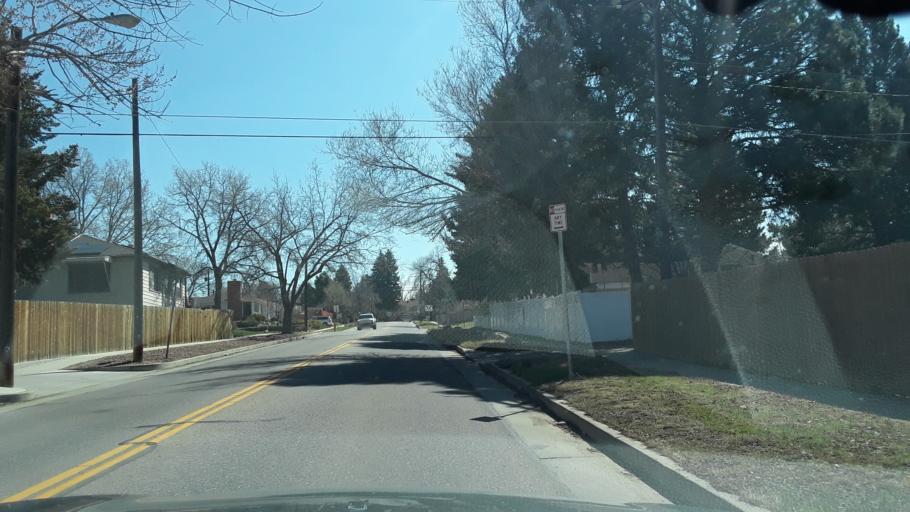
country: US
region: Colorado
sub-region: El Paso County
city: Colorado Springs
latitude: 38.8498
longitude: -104.7965
